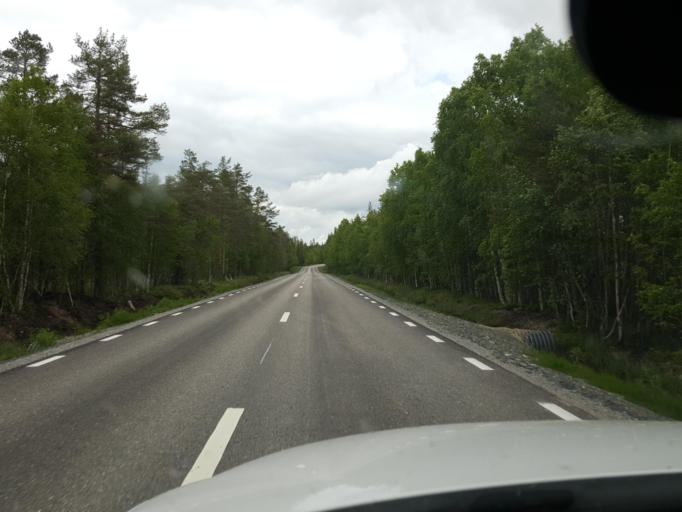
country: SE
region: Gaevleborg
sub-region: Ljusdals Kommun
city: Farila
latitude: 61.7455
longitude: 15.3592
